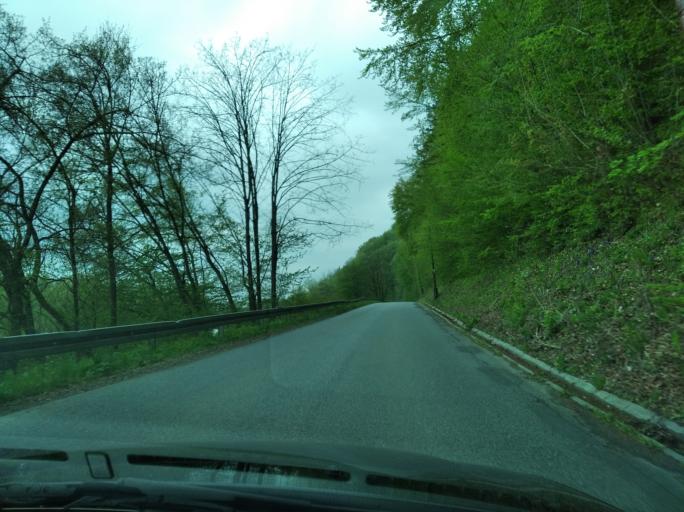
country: PL
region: Subcarpathian Voivodeship
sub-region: Powiat sanocki
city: Sanok
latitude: 49.6030
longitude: 22.1905
